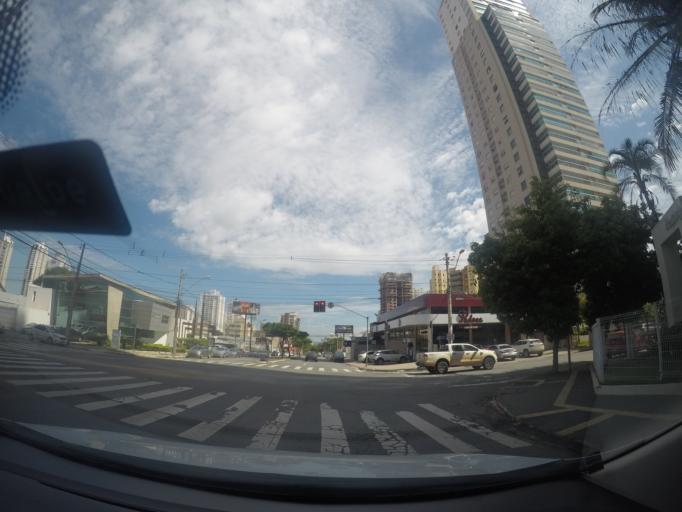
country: BR
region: Goias
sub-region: Goiania
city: Goiania
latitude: -16.7026
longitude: -49.2698
